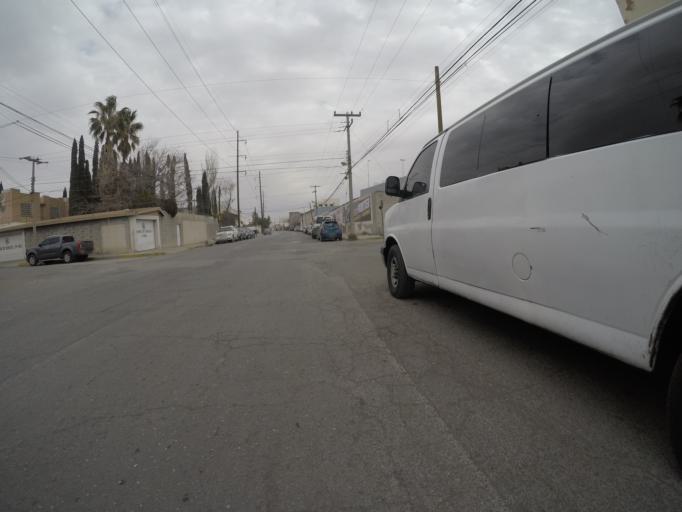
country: MX
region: Chihuahua
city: Ciudad Juarez
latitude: 31.7399
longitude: -106.4321
